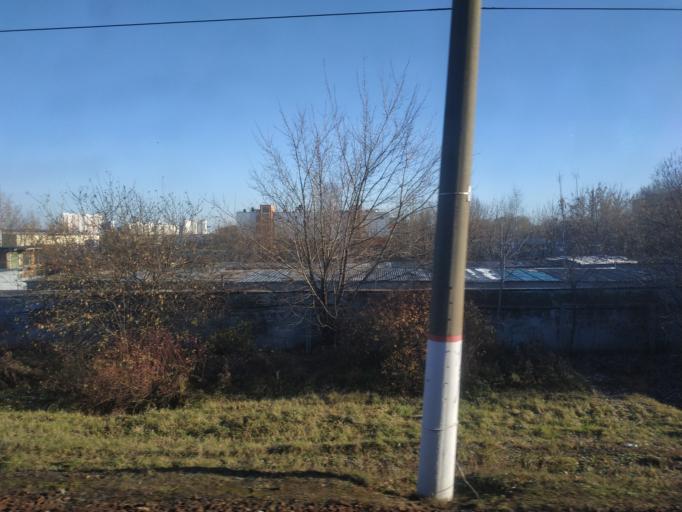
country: RU
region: Moscow
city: Nagornyy
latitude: 55.6354
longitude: 37.6261
